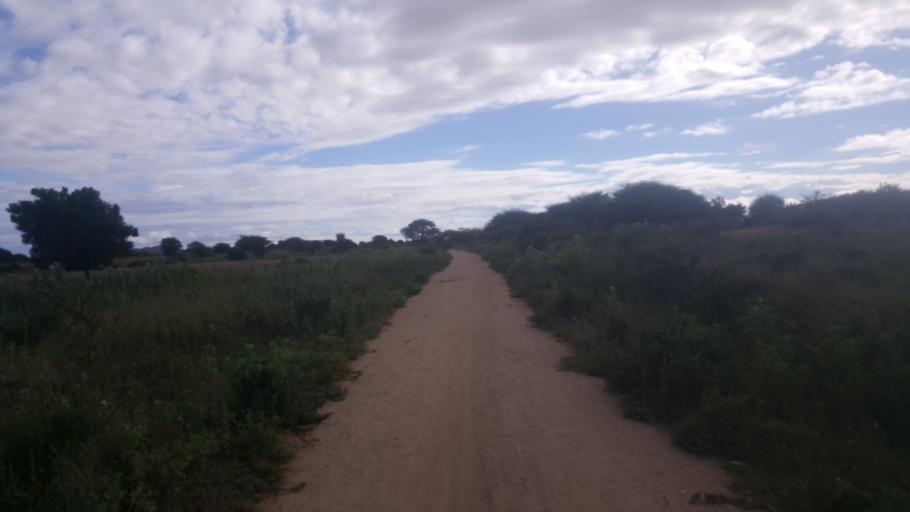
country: TZ
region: Dodoma
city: Dodoma
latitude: -6.0918
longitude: 35.5284
